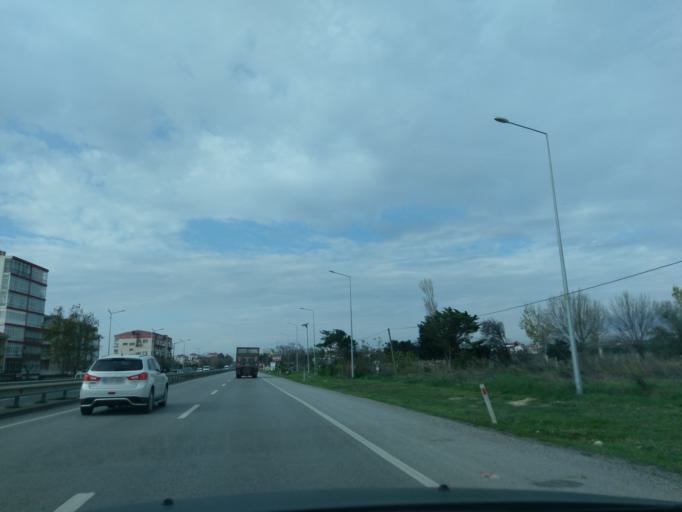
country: TR
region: Istanbul
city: Celaliye
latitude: 41.0472
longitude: 28.4024
